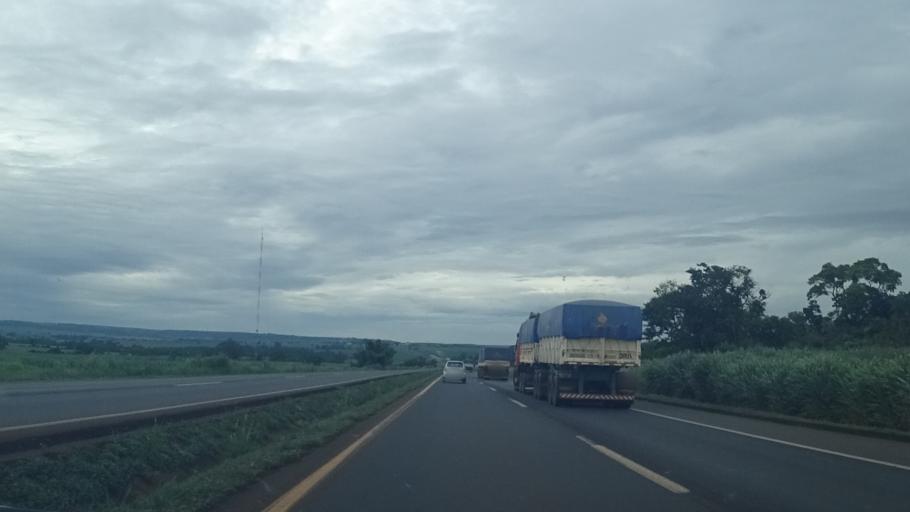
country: BR
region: Minas Gerais
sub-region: Centralina
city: Centralina
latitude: -18.5265
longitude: -49.1913
